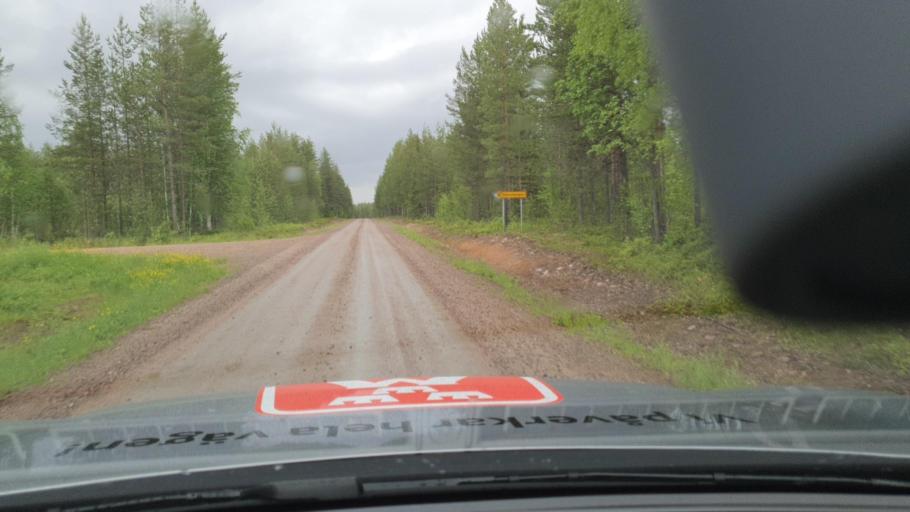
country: SE
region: Norrbotten
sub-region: Overkalix Kommun
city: OEverkalix
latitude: 66.6181
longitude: 22.7296
